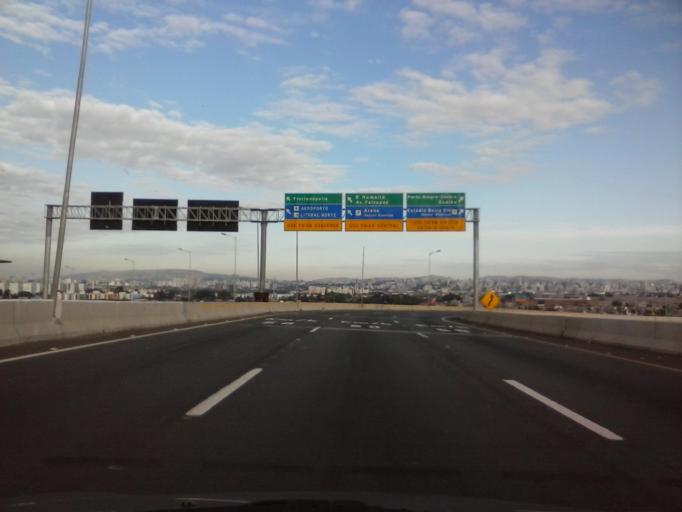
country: BR
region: Rio Grande do Sul
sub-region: Canoas
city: Canoas
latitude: -29.9722
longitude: -51.1995
